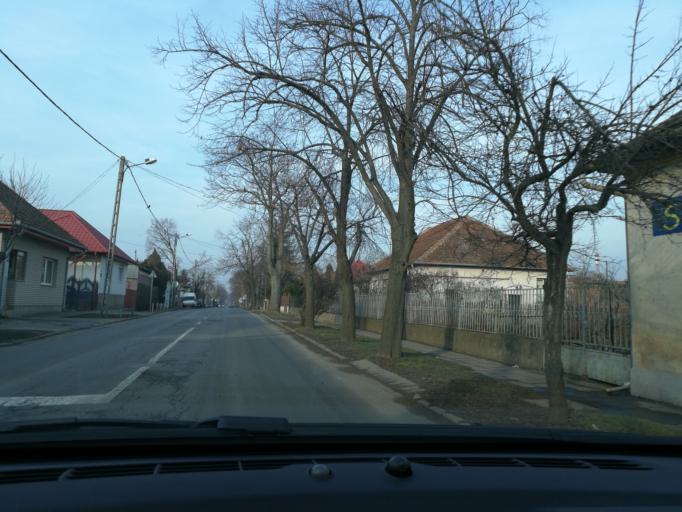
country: HU
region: Szabolcs-Szatmar-Bereg
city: Nyiregyhaza
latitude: 47.9512
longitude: 21.6943
